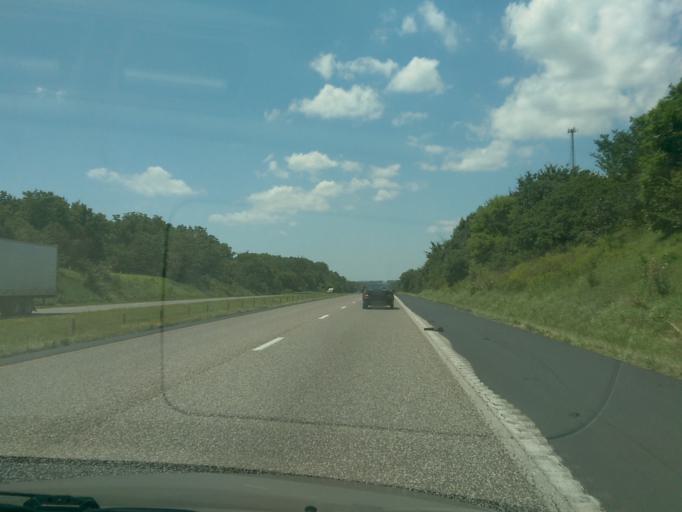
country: US
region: Missouri
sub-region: Cooper County
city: Boonville
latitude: 38.9396
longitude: -92.6038
